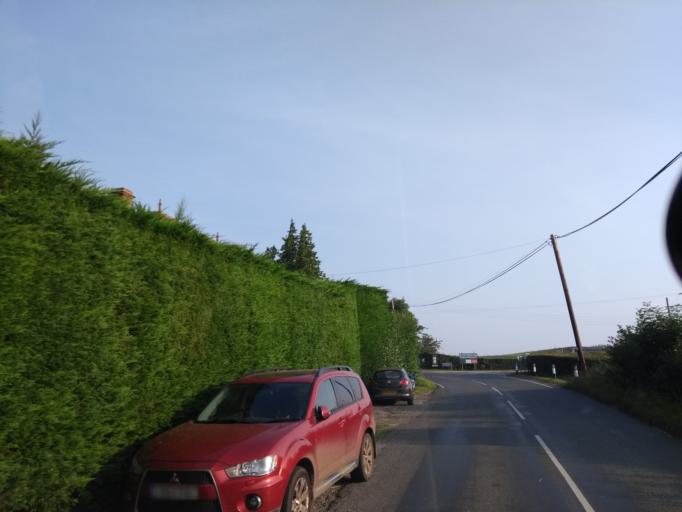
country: GB
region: England
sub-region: Somerset
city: Curry Rivel
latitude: 50.9991
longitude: -2.8609
